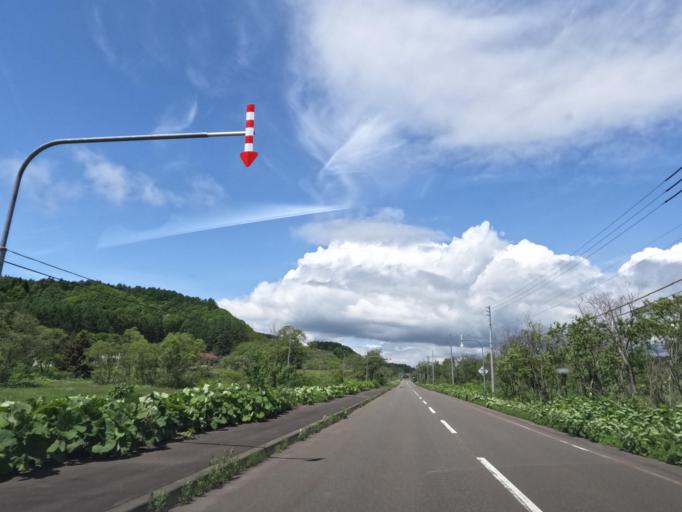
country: JP
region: Hokkaido
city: Tobetsu
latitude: 43.3913
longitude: 141.5792
